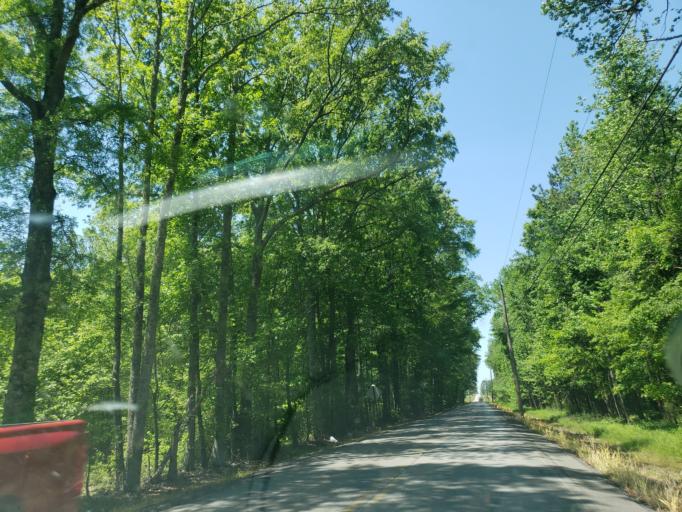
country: US
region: Alabama
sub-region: Madison County
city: Hazel Green
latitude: 34.9617
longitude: -86.5881
